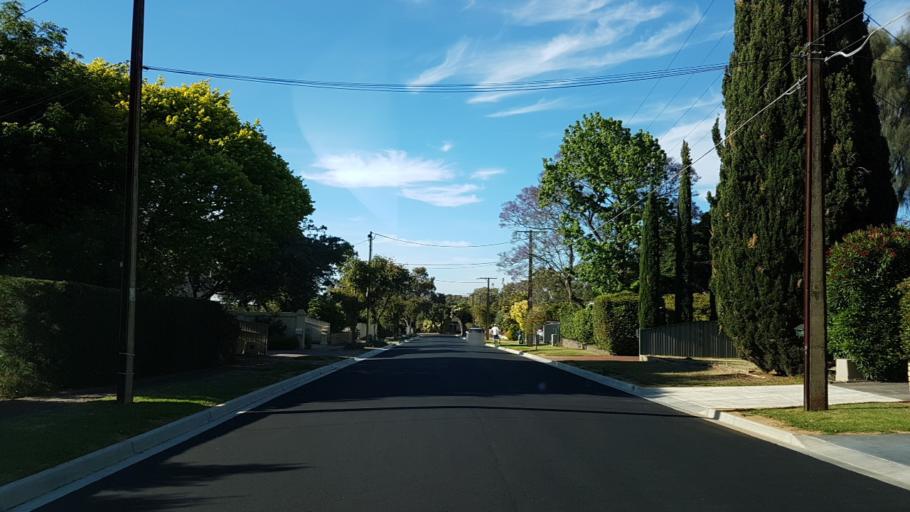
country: AU
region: South Australia
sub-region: Campbelltown
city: Campbelltown
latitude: -34.8988
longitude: 138.6809
